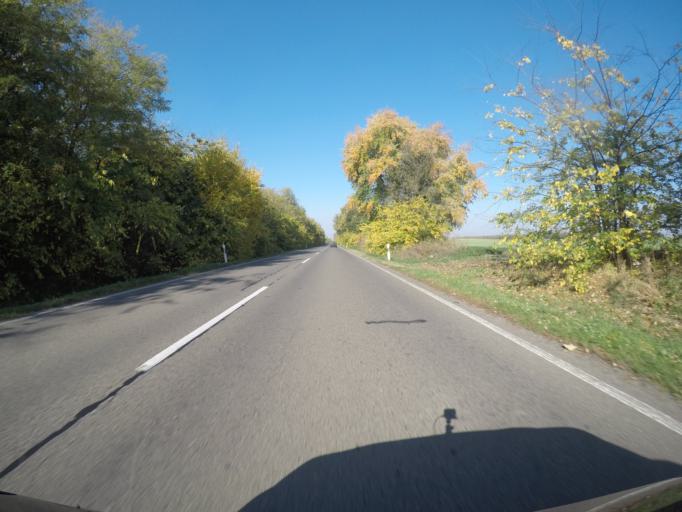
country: HU
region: Tolna
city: Szedres
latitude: 46.5198
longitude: 18.6617
